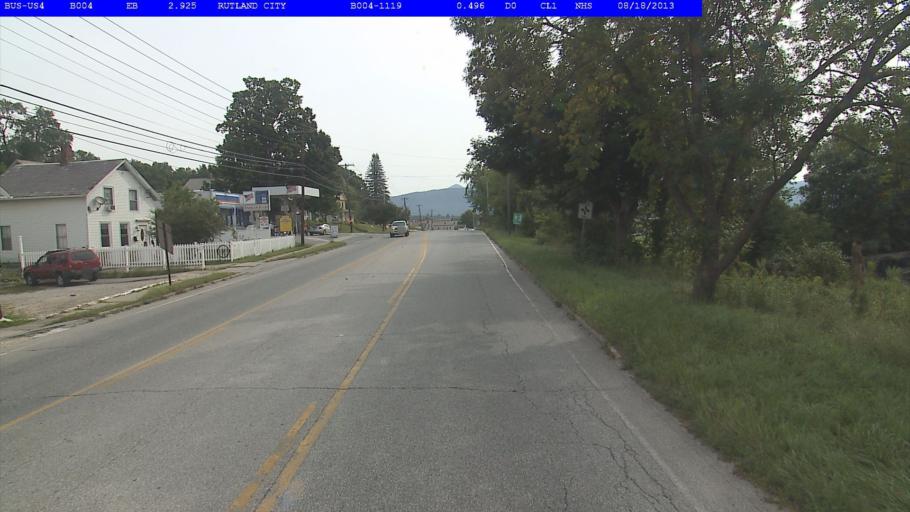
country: US
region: Vermont
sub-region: Rutland County
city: Rutland
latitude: 43.6051
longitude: -72.9975
